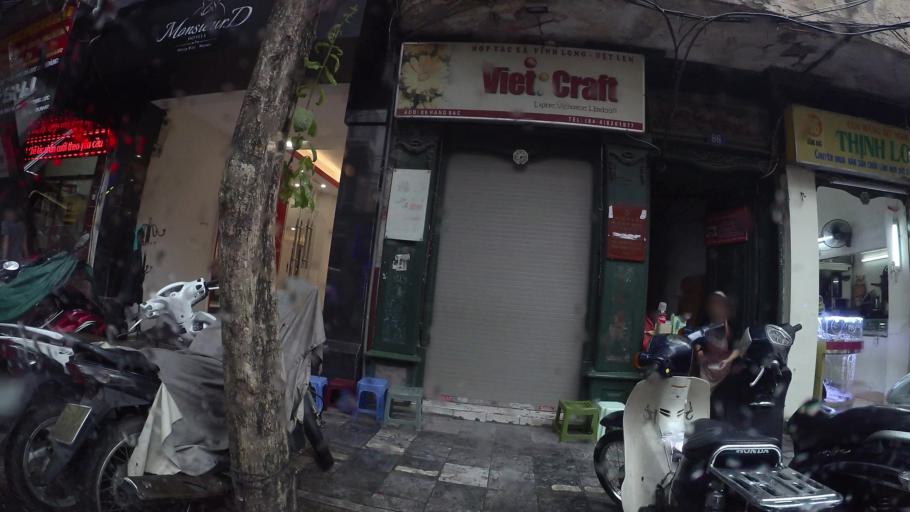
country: VN
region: Ha Noi
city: Hoan Kiem
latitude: 21.0341
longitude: 105.8521
